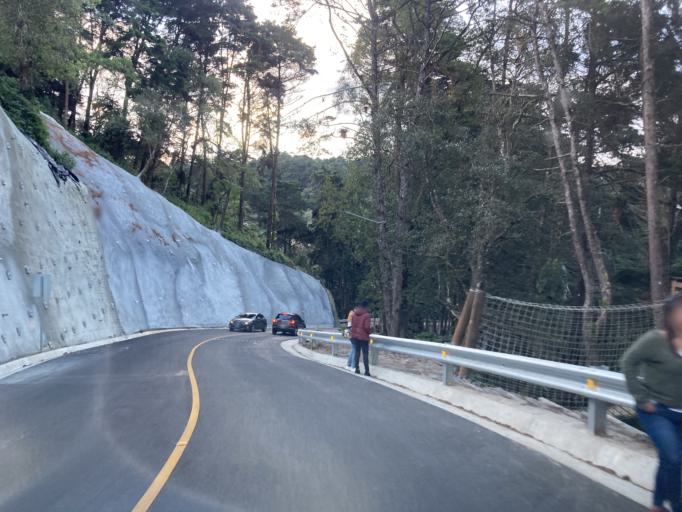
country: GT
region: Guatemala
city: Santa Catarina Pinula
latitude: 14.5575
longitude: -90.4636
